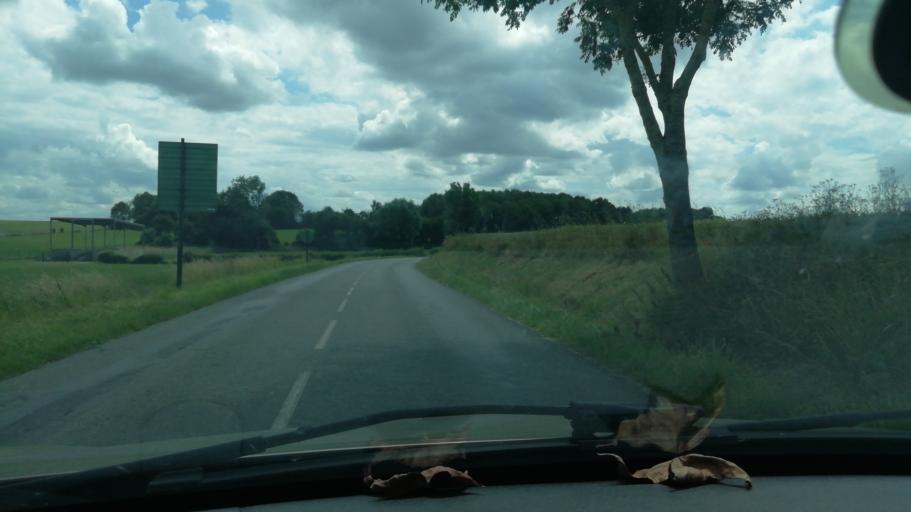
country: FR
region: Nord-Pas-de-Calais
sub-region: Departement du Pas-de-Calais
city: Aubigny-en-Artois
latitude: 50.3411
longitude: 2.5908
